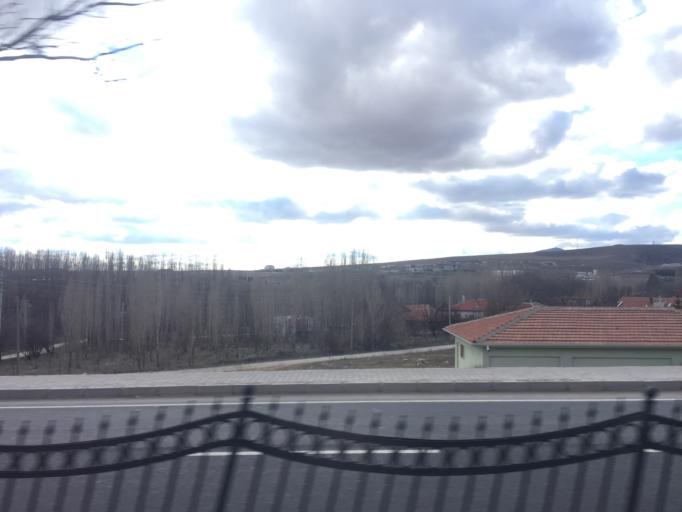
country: TR
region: Kirsehir
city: Kirsehir
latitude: 39.1687
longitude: 34.1513
